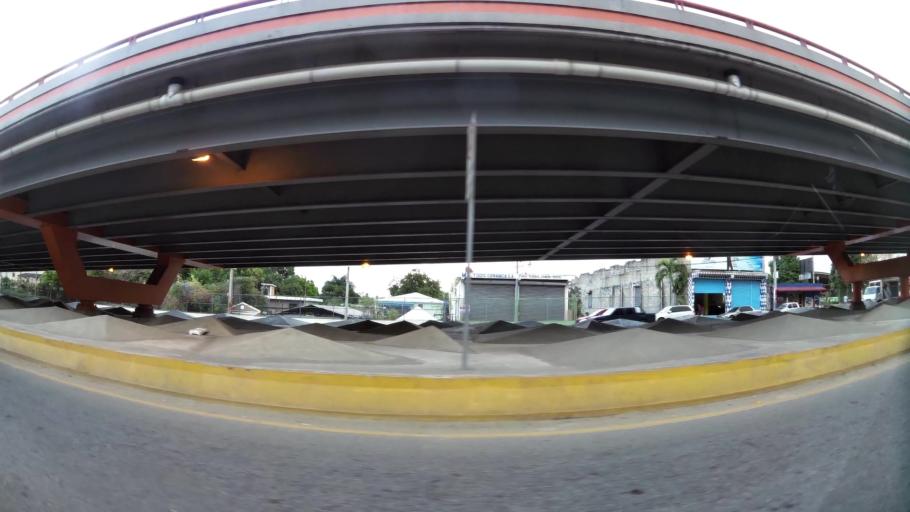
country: DO
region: Santo Domingo
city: Santo Domingo Oeste
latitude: 18.5226
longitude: -70.0105
